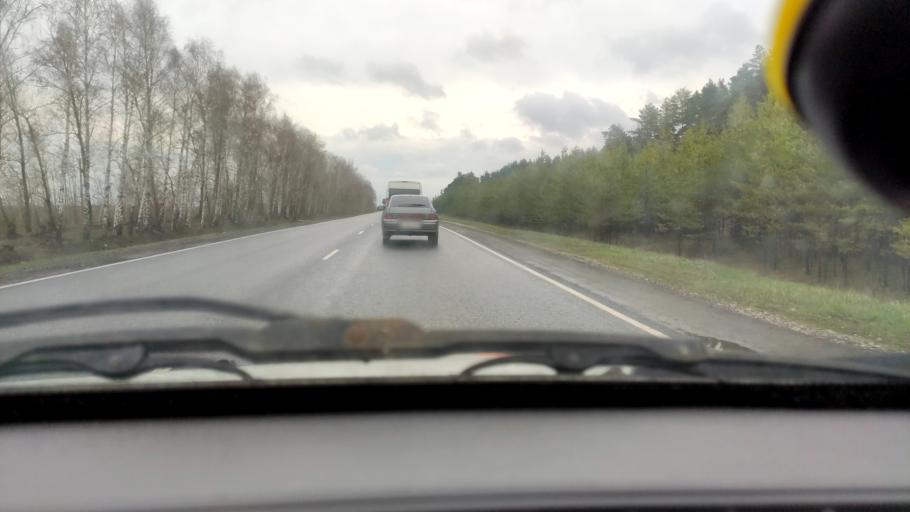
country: RU
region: Samara
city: Povolzhskiy
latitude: 53.6262
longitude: 49.6523
